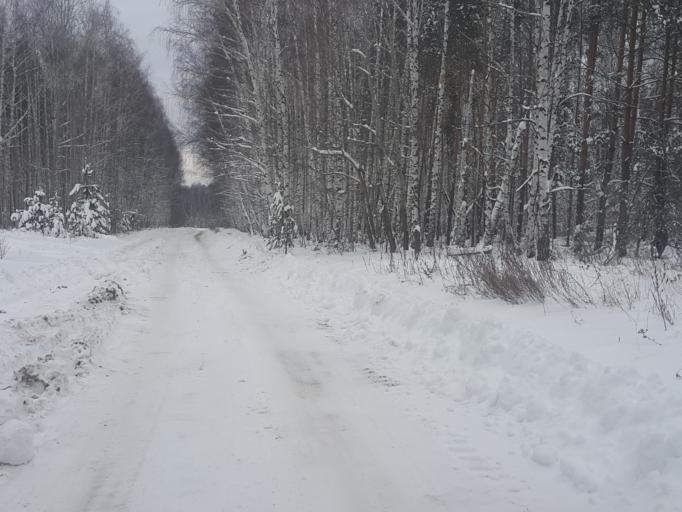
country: RU
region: Tambov
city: Platonovka
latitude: 52.8879
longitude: 41.8549
